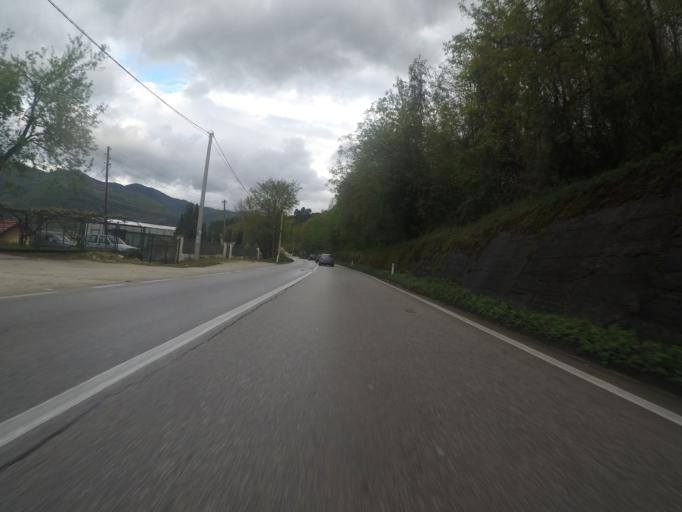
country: BA
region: Federation of Bosnia and Herzegovina
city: Konjic
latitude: 43.6851
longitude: 17.8799
